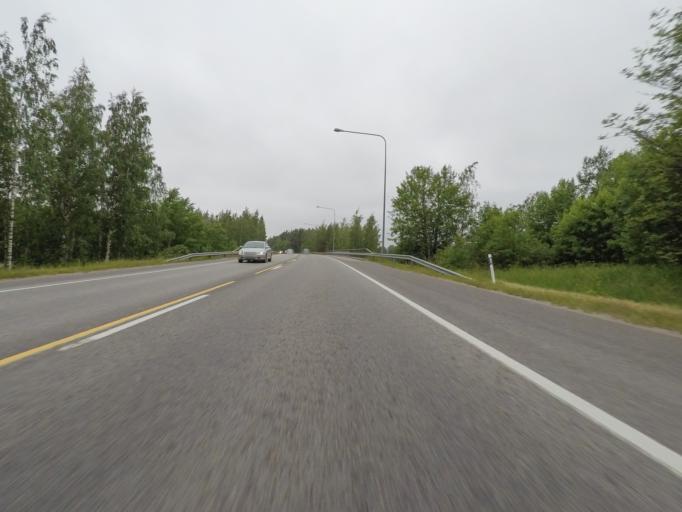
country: FI
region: Varsinais-Suomi
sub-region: Turku
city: Raisio
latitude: 60.4612
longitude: 22.1743
